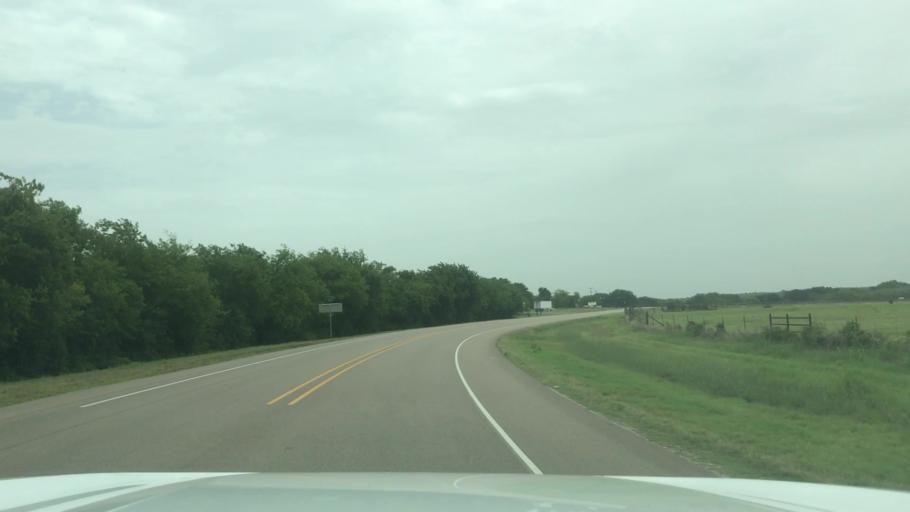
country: US
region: Texas
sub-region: Hamilton County
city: Hico
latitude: 31.9830
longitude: -97.8668
